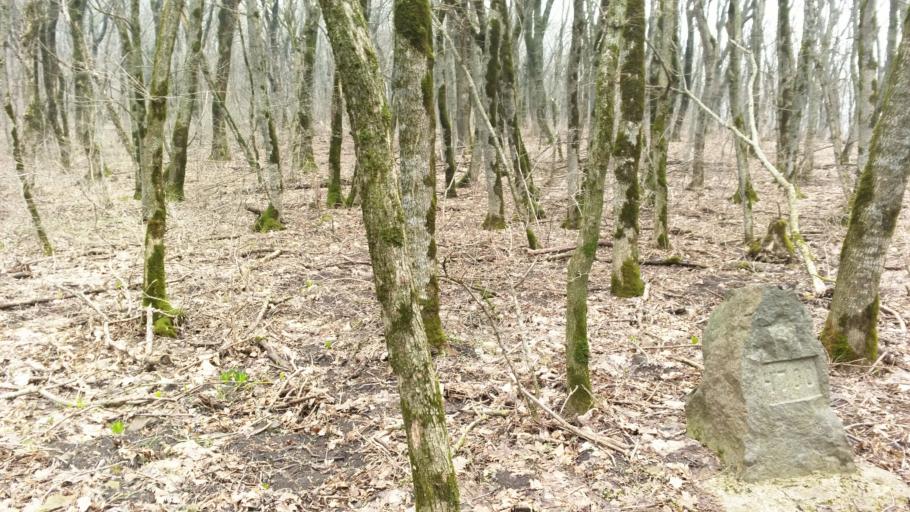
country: RU
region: Stavropol'skiy
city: Zheleznovodsk
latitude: 44.1555
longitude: 43.0422
